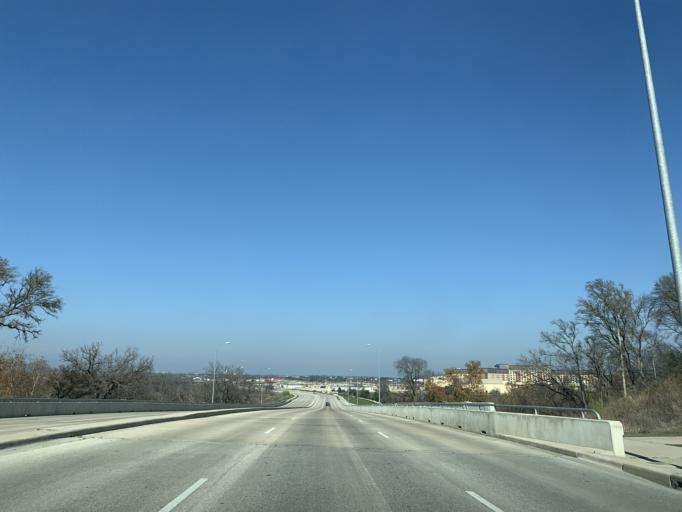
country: US
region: Texas
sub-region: Williamson County
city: Round Rock
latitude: 30.5118
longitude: -97.6364
